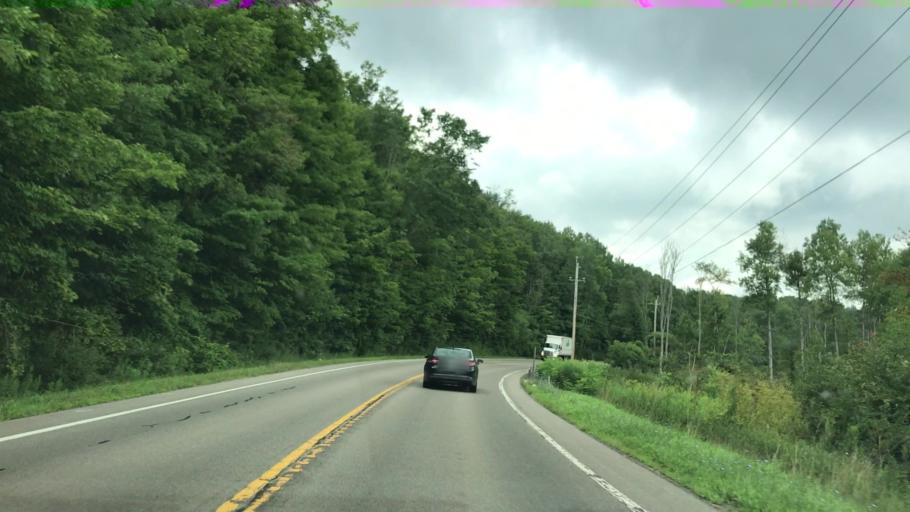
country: US
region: New York
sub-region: Steuben County
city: Bath
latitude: 42.4028
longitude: -77.3503
